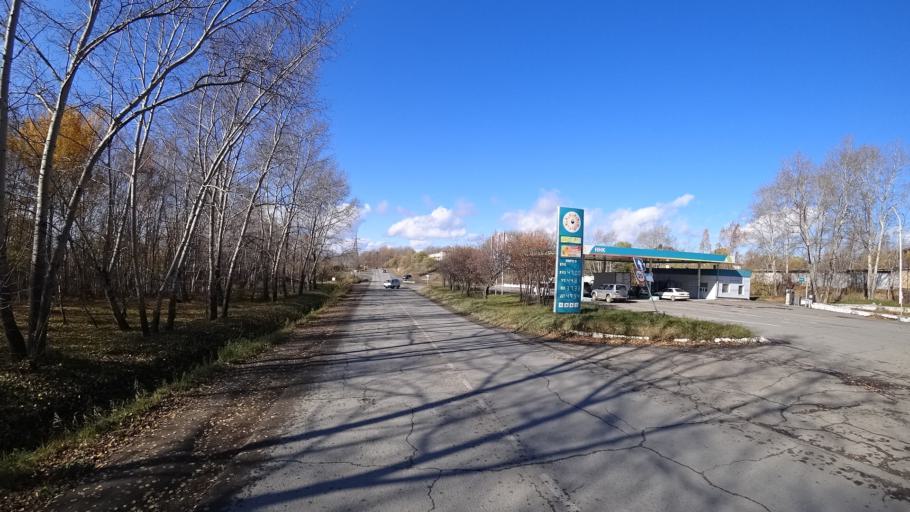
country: RU
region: Khabarovsk Krai
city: Amursk
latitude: 50.2322
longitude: 136.8993
